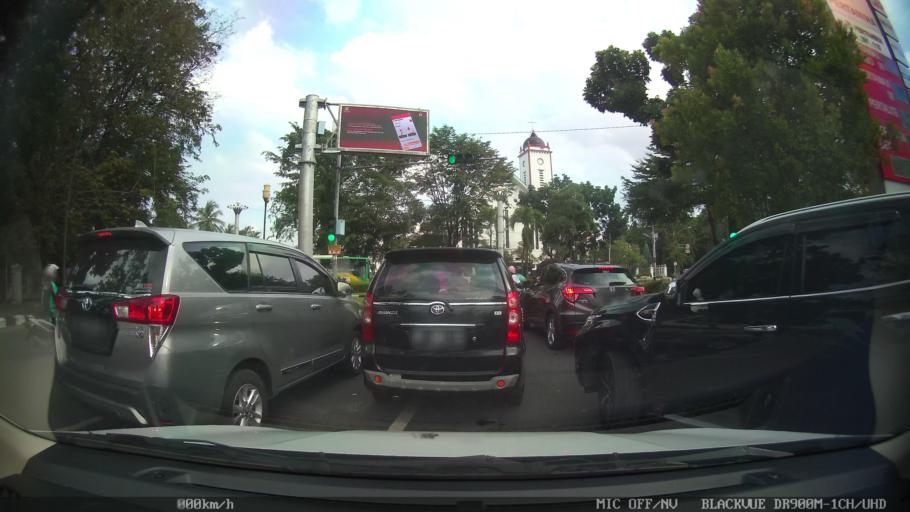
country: ID
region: North Sumatra
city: Medan
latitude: 3.5783
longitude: 98.6772
